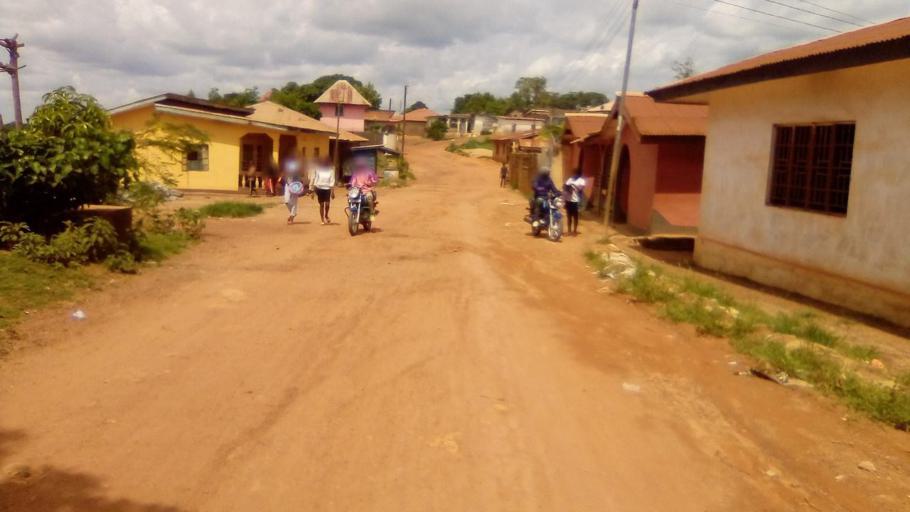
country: SL
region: Southern Province
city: Bo
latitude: 7.9678
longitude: -11.7280
